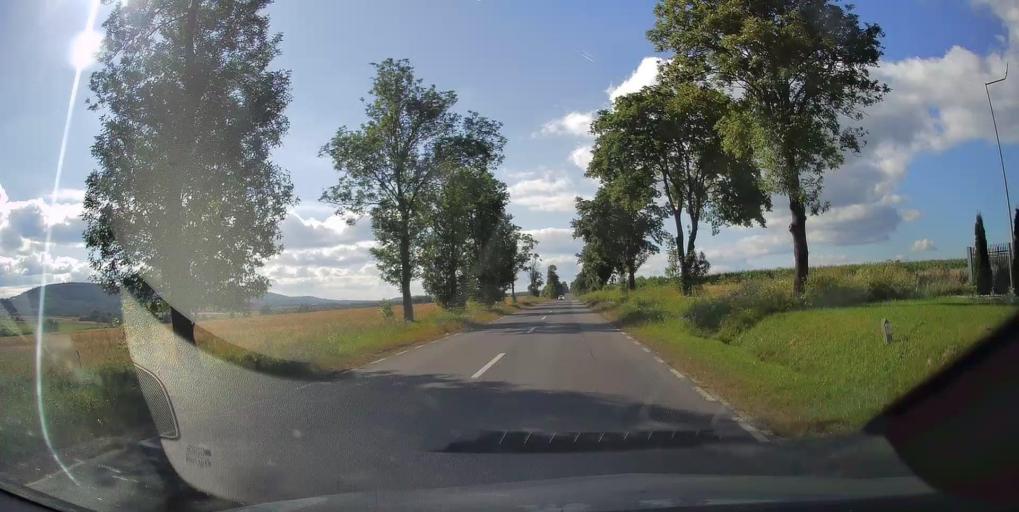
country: PL
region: Swietokrzyskie
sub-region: Powiat kielecki
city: Bodzentyn
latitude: 50.9513
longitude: 20.9259
